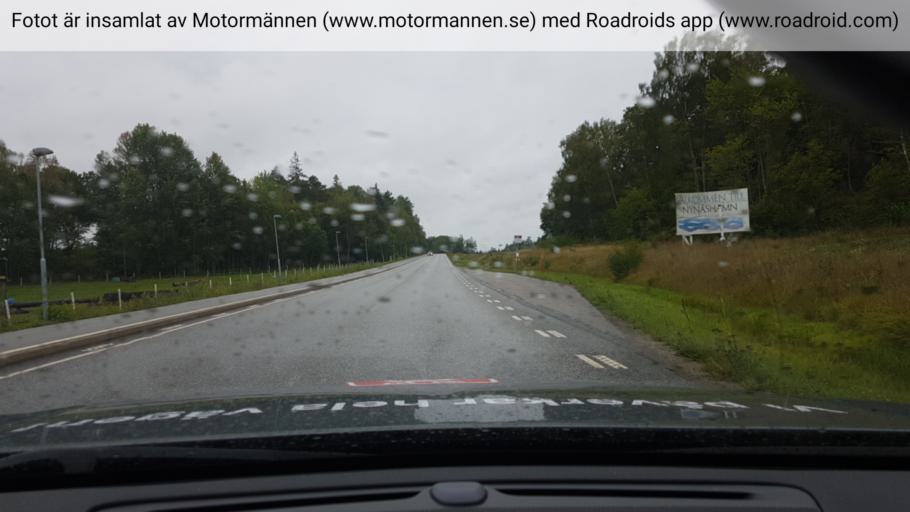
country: SE
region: Stockholm
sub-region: Nynashamns Kommun
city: Nynashamn
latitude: 58.9297
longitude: 17.9212
